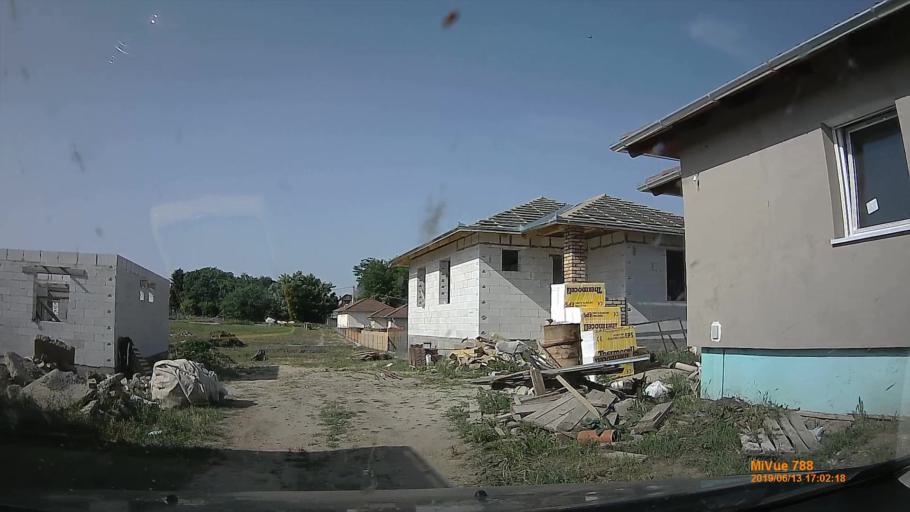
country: HU
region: Pest
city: Gyomro
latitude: 47.4156
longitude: 19.3999
